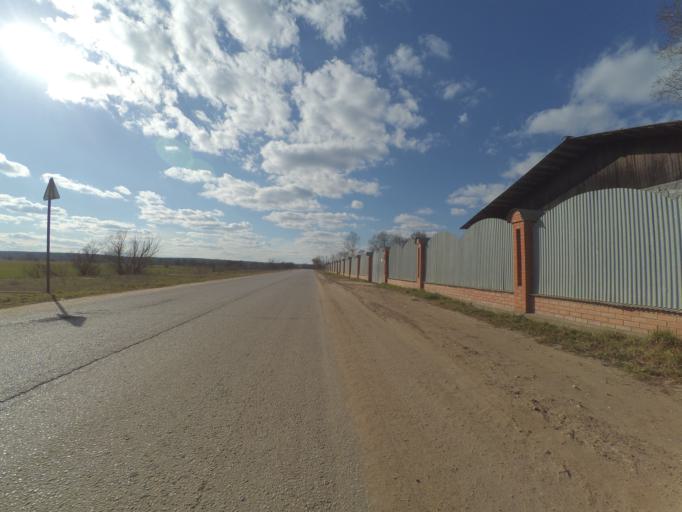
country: RU
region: Moskovskaya
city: Bol'shoye Gryzlovo
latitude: 54.8691
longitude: 37.8411
